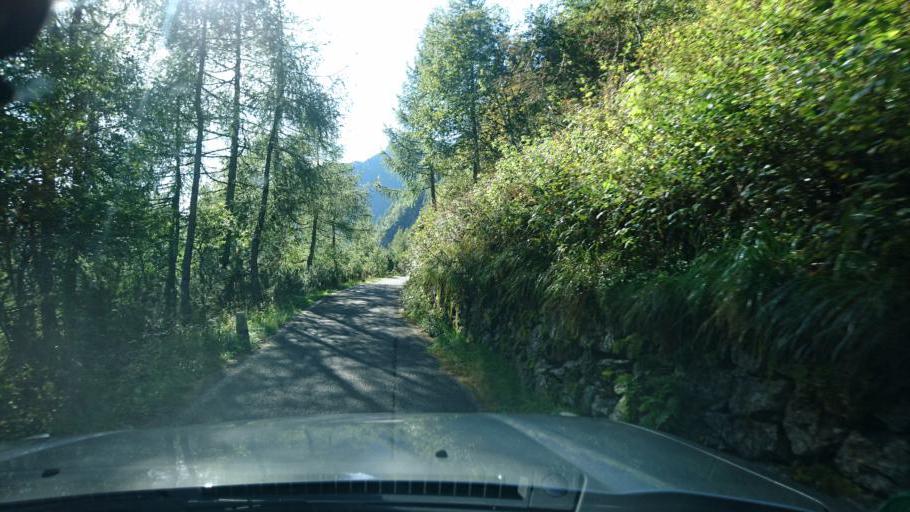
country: IT
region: Lombardy
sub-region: Provincia di Bergamo
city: Schilpario
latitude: 46.0485
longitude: 10.2179
